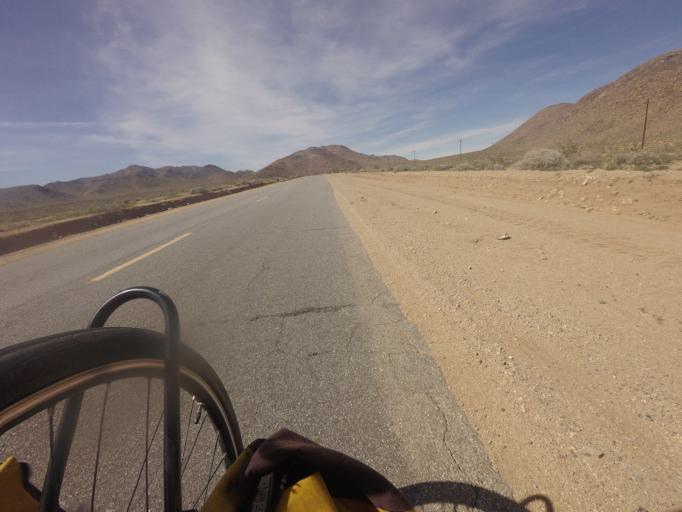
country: US
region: California
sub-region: San Bernardino County
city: Searles Valley
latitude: 35.5779
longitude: -117.4561
